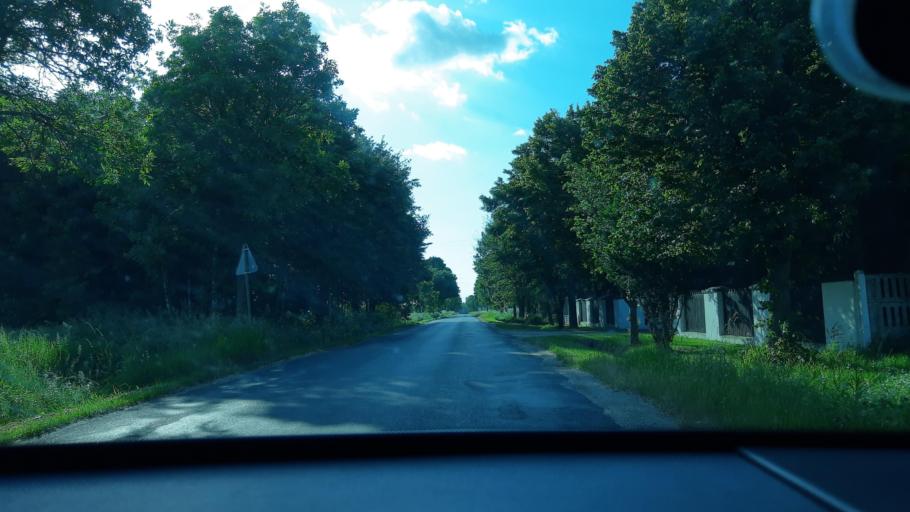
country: PL
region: Lodz Voivodeship
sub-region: Powiat sieradzki
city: Sieradz
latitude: 51.5513
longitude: 18.7691
